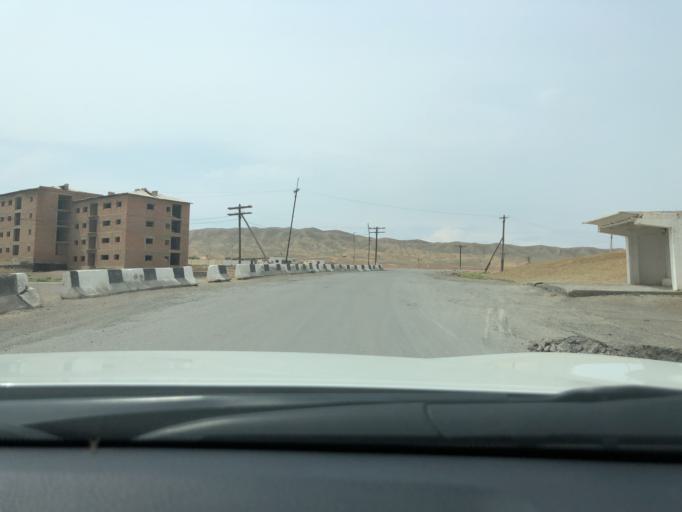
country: TJ
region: Viloyati Sughd
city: Kim
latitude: 40.2089
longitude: 70.4754
